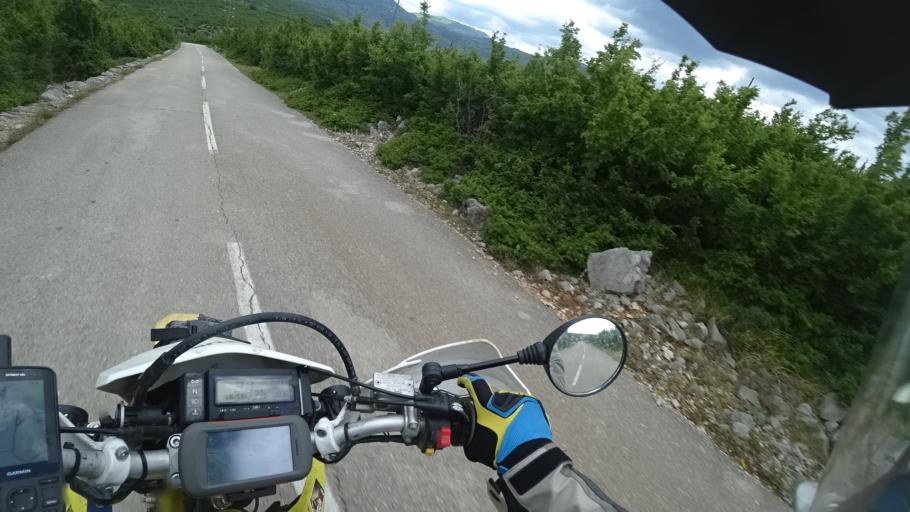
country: HR
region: Zadarska
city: Gracac
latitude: 44.1879
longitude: 15.8884
